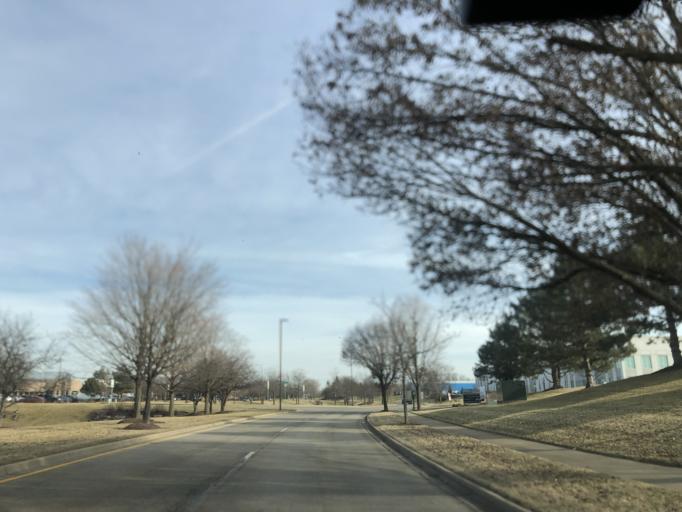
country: US
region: Illinois
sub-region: Cook County
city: Lemont
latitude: 41.6962
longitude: -88.0145
